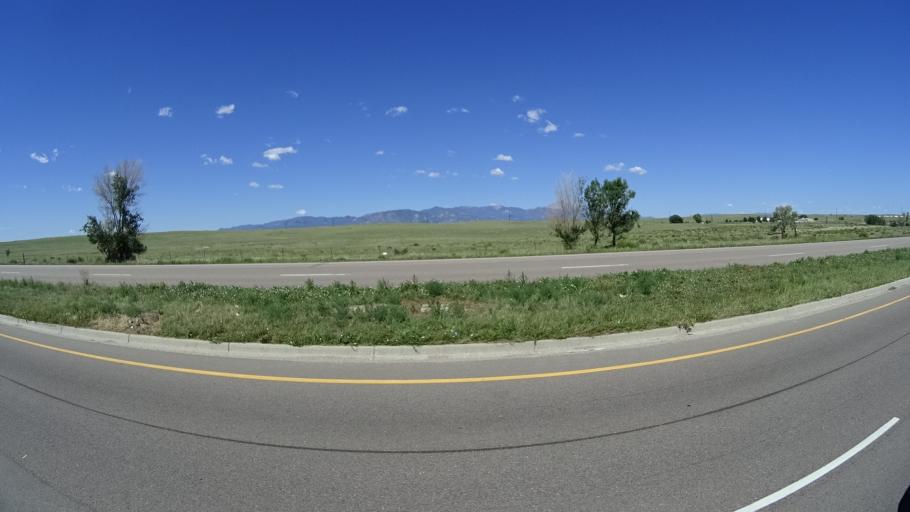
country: US
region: Colorado
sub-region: El Paso County
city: Security-Widefield
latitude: 38.7584
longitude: -104.6597
